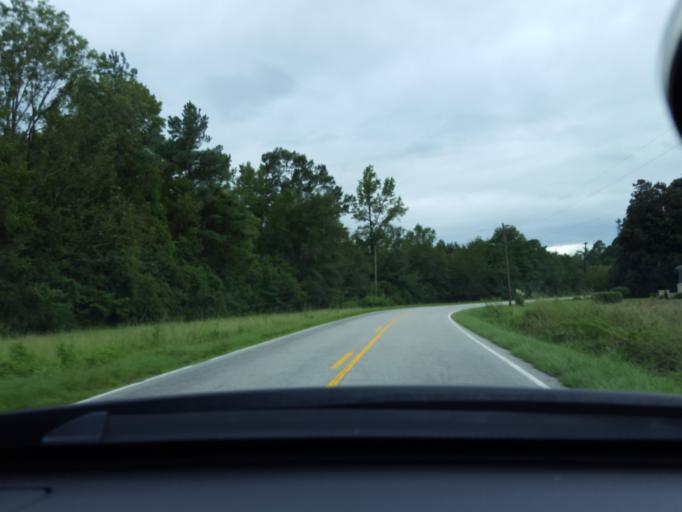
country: US
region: North Carolina
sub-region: Sampson County
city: Roseboro
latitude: 34.7840
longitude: -78.3829
